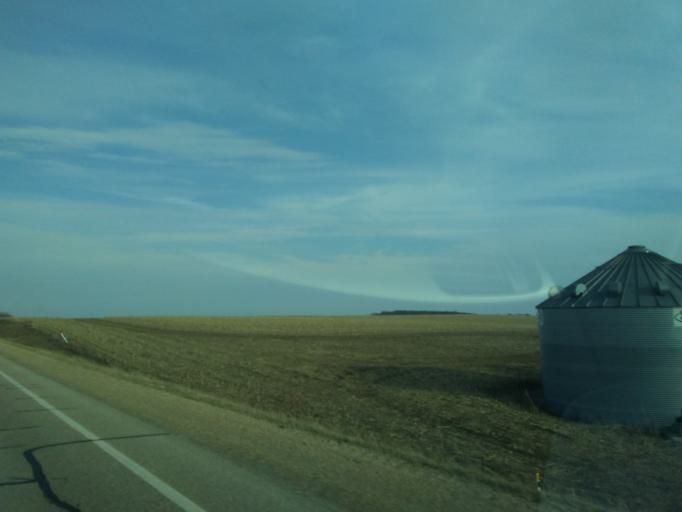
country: US
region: Wisconsin
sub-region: Grant County
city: Fennimore
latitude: 42.9736
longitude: -90.5151
